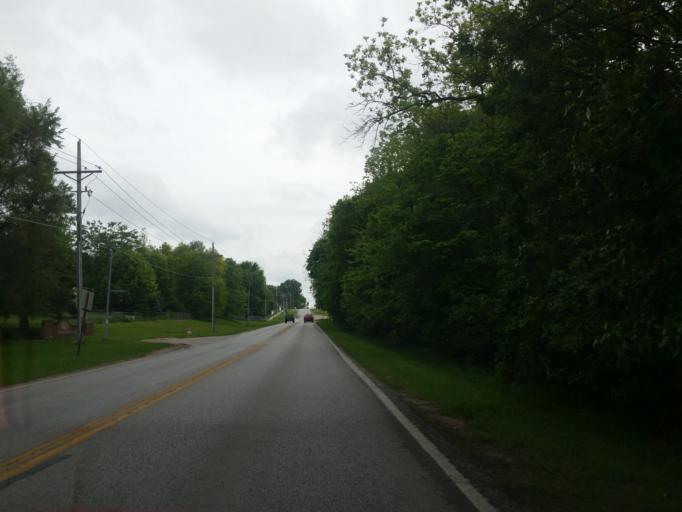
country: US
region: Nebraska
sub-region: Sarpy County
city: Offutt Air Force Base
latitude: 41.1132
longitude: -95.9666
